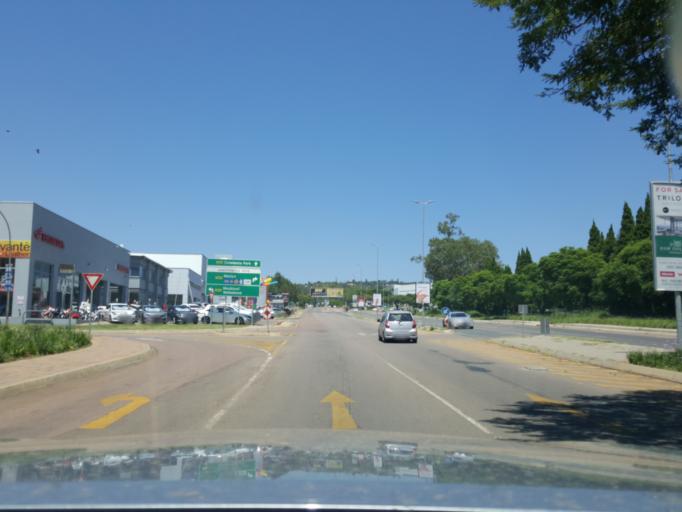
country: ZA
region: Gauteng
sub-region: City of Tshwane Metropolitan Municipality
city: Pretoria
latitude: -25.7906
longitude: 28.2823
